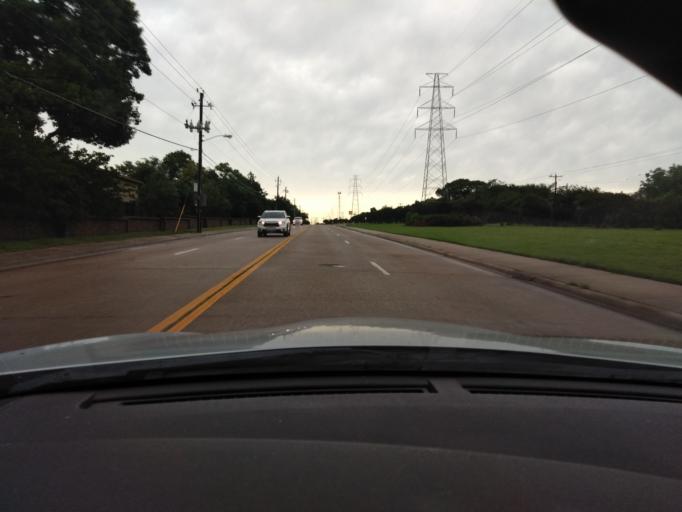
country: US
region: Texas
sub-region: Dallas County
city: Addison
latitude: 32.9632
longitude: -96.7786
